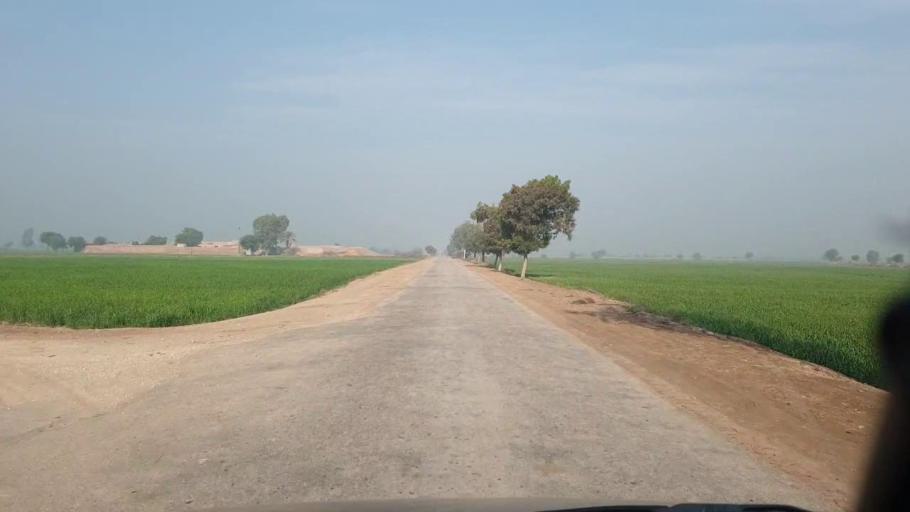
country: PK
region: Sindh
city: Shahdadpur
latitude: 25.9785
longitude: 68.5734
